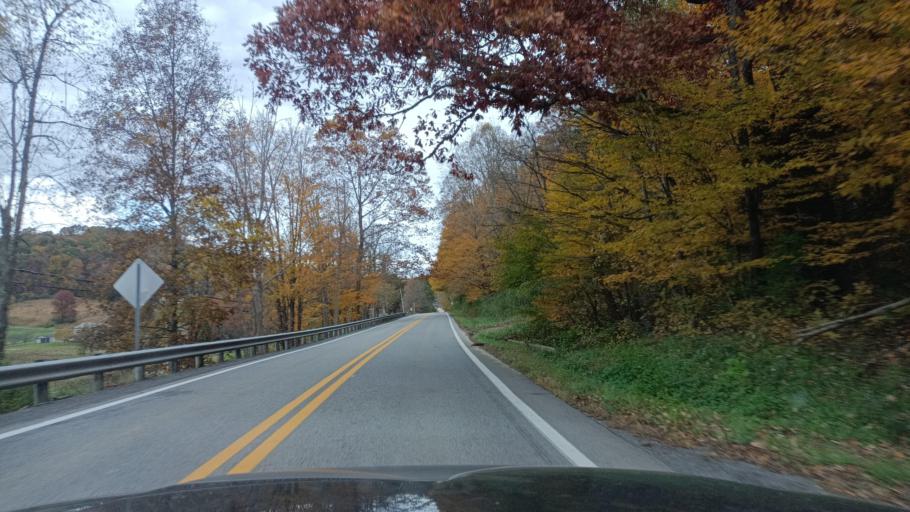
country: US
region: West Virginia
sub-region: Taylor County
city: Grafton
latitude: 39.3596
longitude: -79.9920
